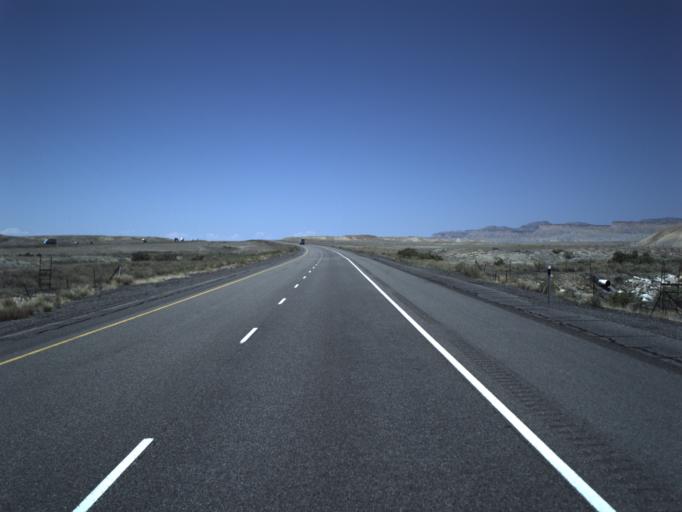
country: US
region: Utah
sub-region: Grand County
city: Moab
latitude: 38.9421
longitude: -109.5233
